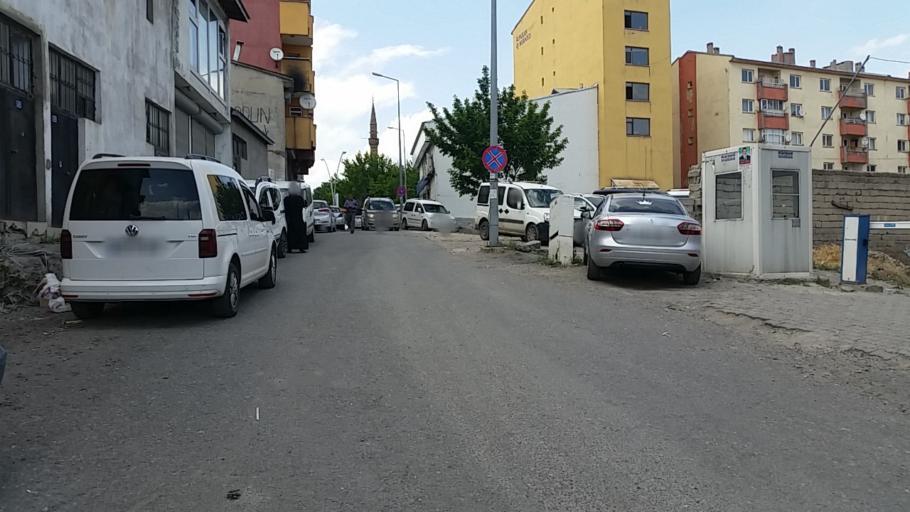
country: TR
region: Agri
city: Agri
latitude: 39.7183
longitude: 43.0518
